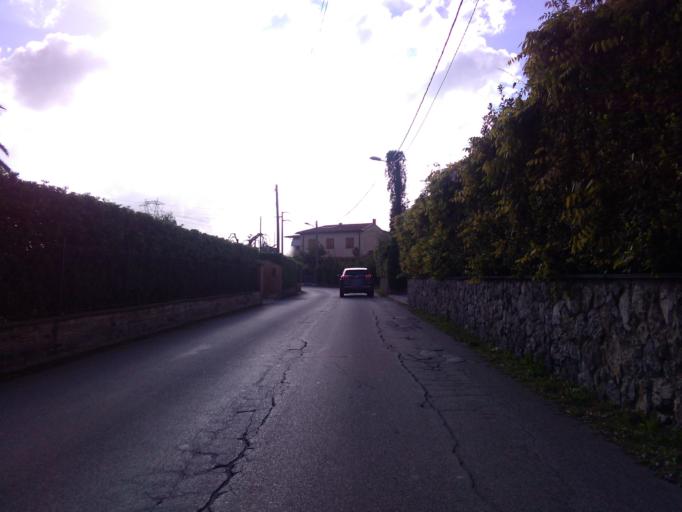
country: IT
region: Tuscany
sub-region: Provincia di Lucca
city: Ripa-Pozzi-Querceta-Ponterosso
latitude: 43.9868
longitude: 10.2056
